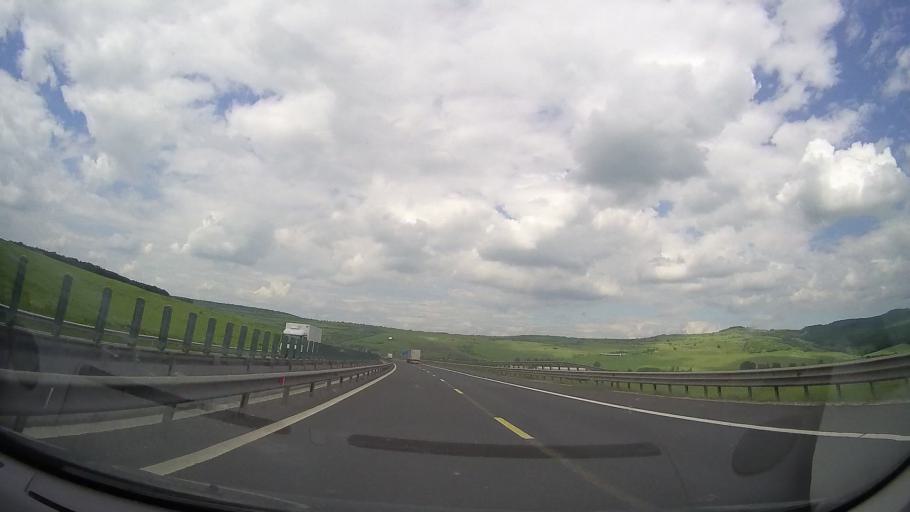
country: RO
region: Sibiu
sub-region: Comuna Apoldu de Jos
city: Apoldu de Jos
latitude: 45.8614
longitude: 23.8797
